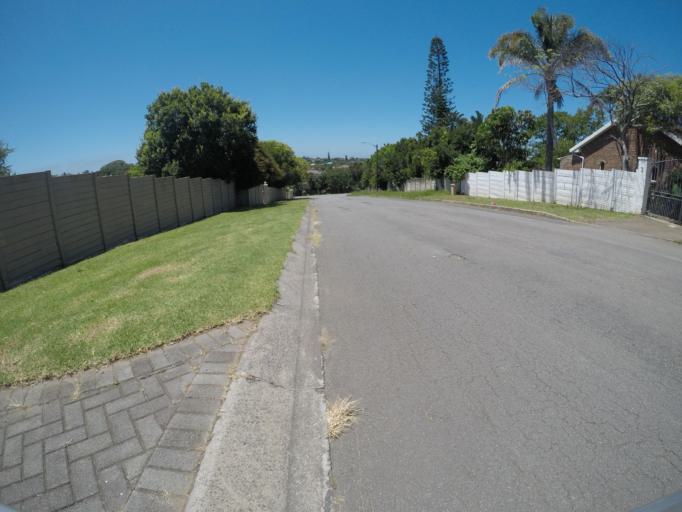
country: ZA
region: Eastern Cape
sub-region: Buffalo City Metropolitan Municipality
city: East London
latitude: -32.9644
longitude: 27.9360
